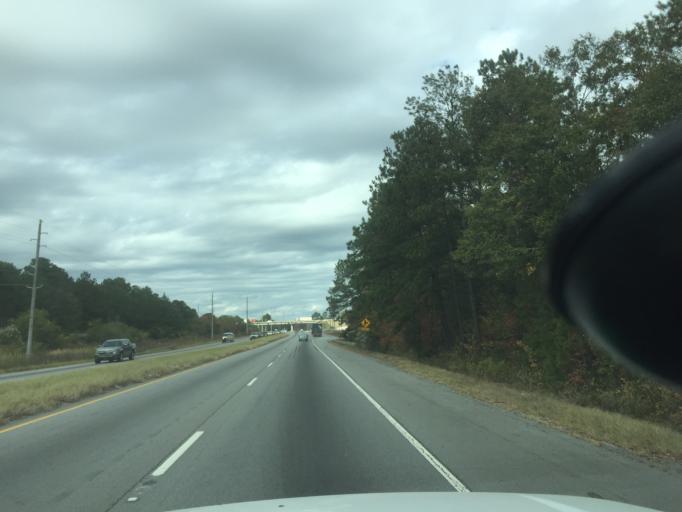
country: US
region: Georgia
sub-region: Chatham County
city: Port Wentworth
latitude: 32.1585
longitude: -81.1824
